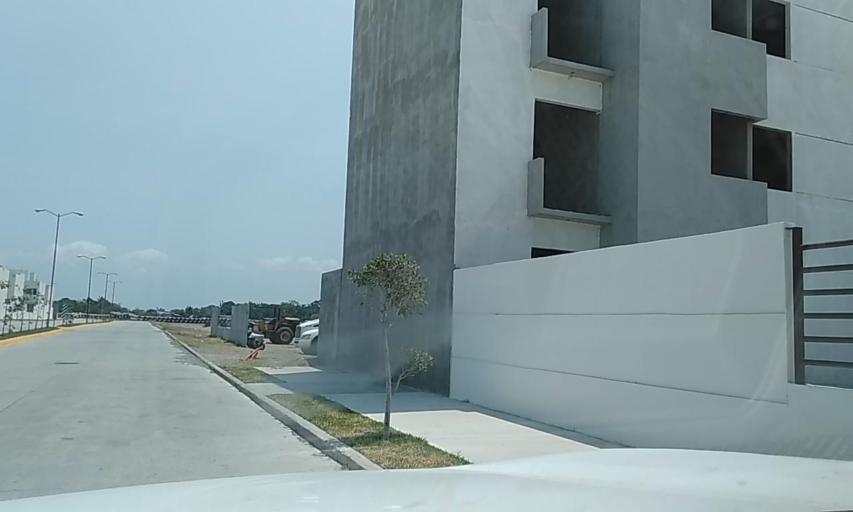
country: MX
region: Veracruz
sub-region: Veracruz
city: Hacienda Sotavento
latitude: 19.1237
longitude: -96.1713
